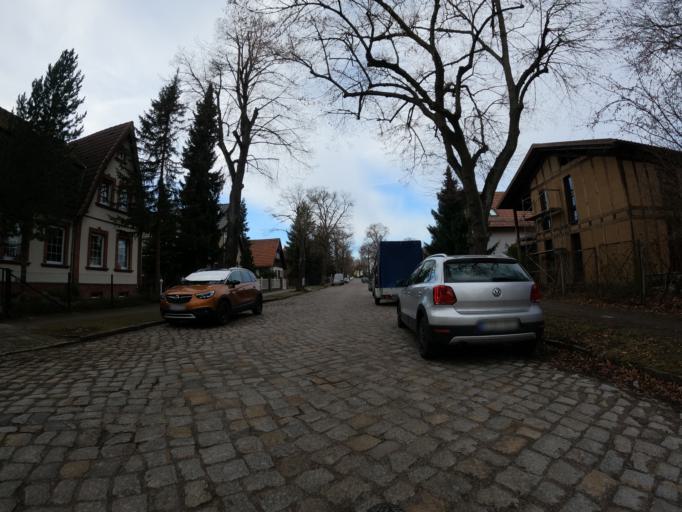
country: DE
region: Berlin
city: Mahlsdorf
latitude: 52.5147
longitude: 13.6211
